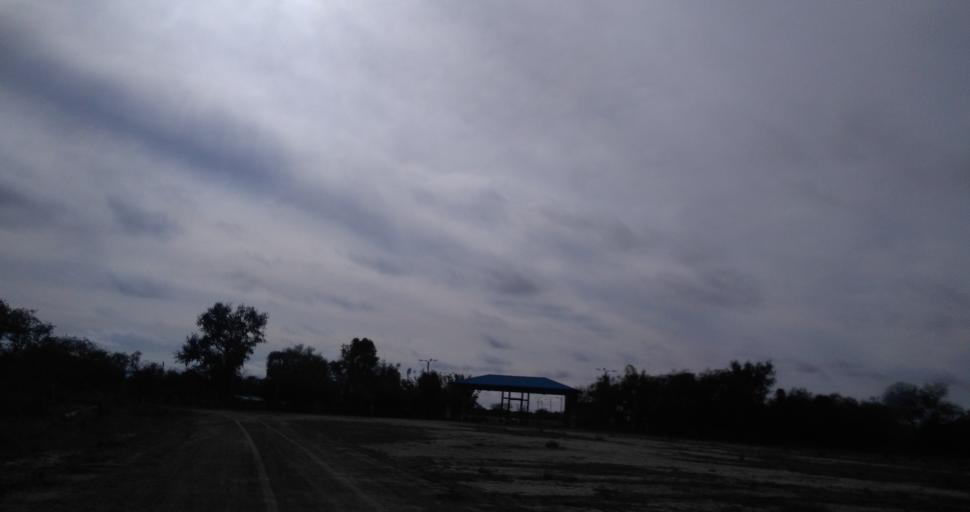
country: AR
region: Chaco
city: Fontana
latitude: -27.3901
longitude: -58.9847
